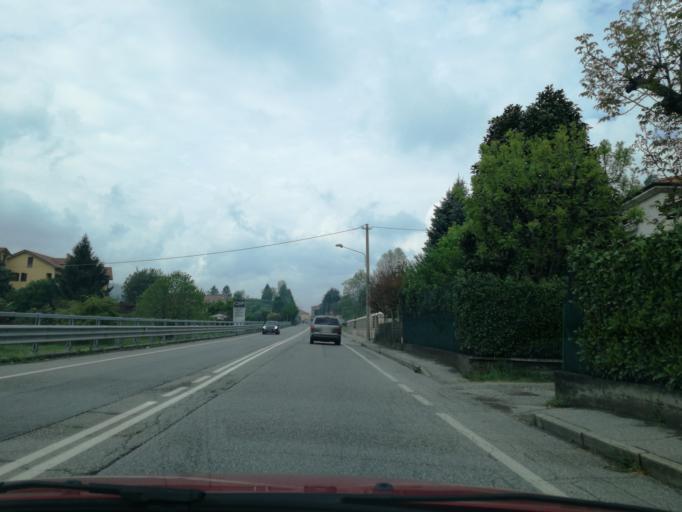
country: IT
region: Lombardy
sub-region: Provincia di Lecco
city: Rovagnate
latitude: 45.7356
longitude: 9.3809
